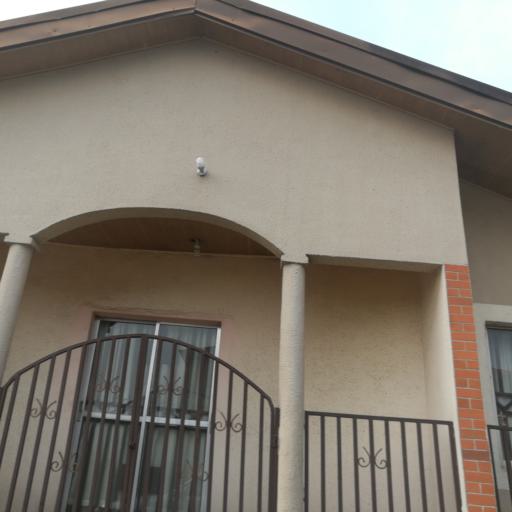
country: NG
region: Rivers
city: Port Harcourt
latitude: 4.8477
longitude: 7.0550
